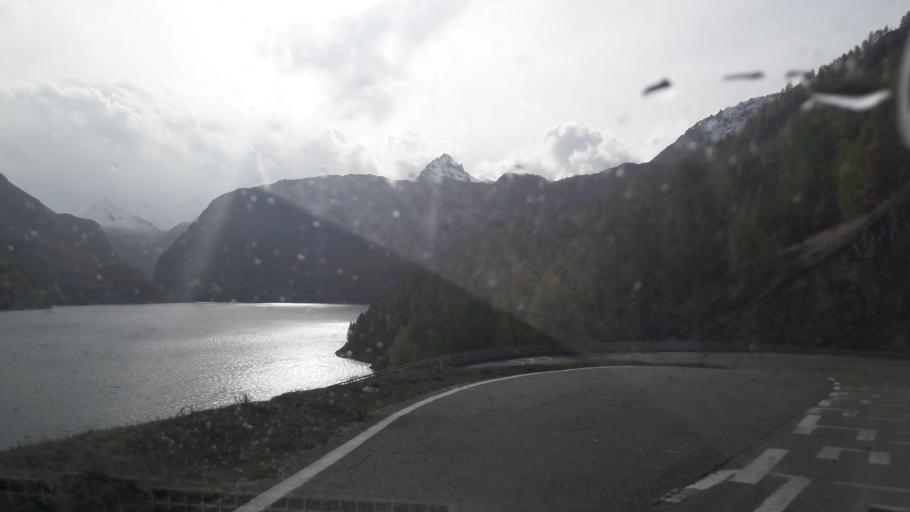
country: FR
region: Rhone-Alpes
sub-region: Departement de la Savoie
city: Tignes
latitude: 45.4928
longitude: 6.9258
